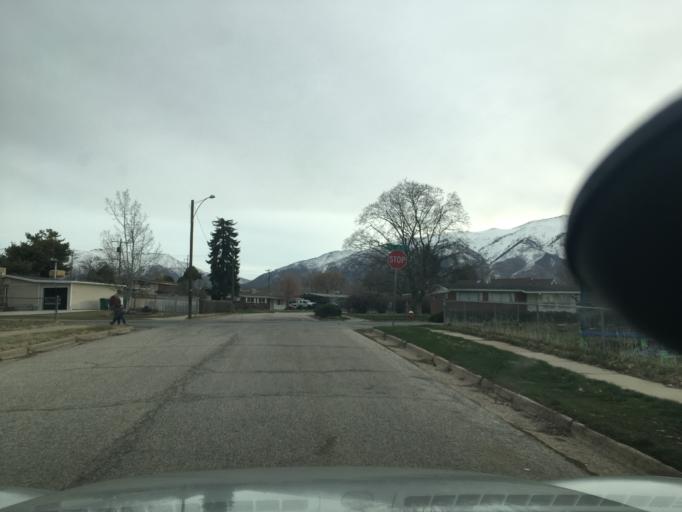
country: US
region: Utah
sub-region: Davis County
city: Layton
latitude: 41.0733
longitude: -111.9674
